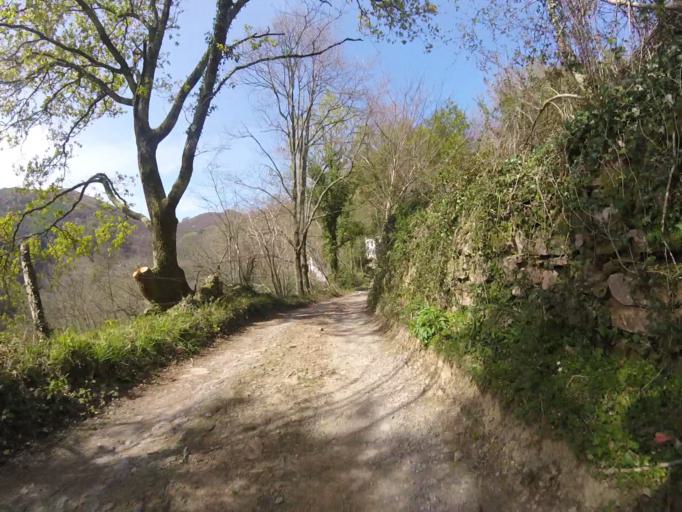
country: ES
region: Basque Country
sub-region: Provincia de Guipuzcoa
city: Irun
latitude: 43.2711
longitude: -1.8112
